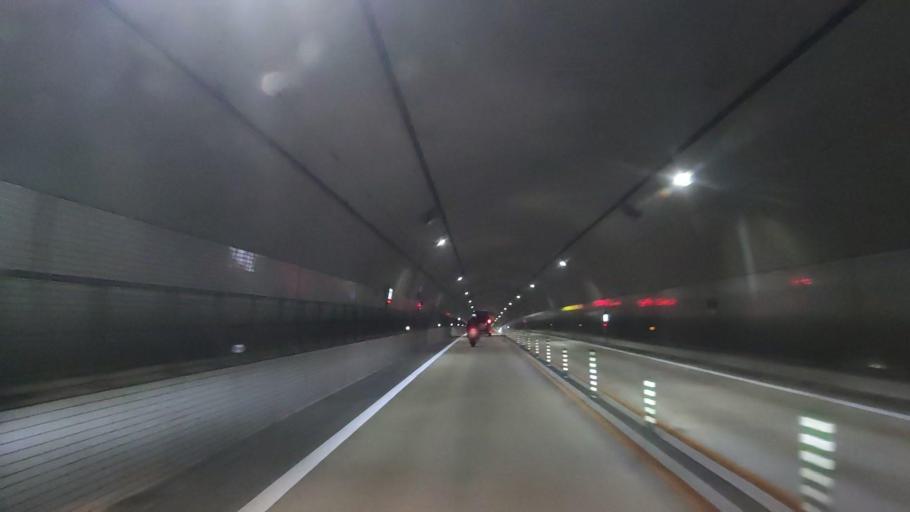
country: JP
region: Shizuoka
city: Ito
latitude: 34.9425
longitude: 138.9435
